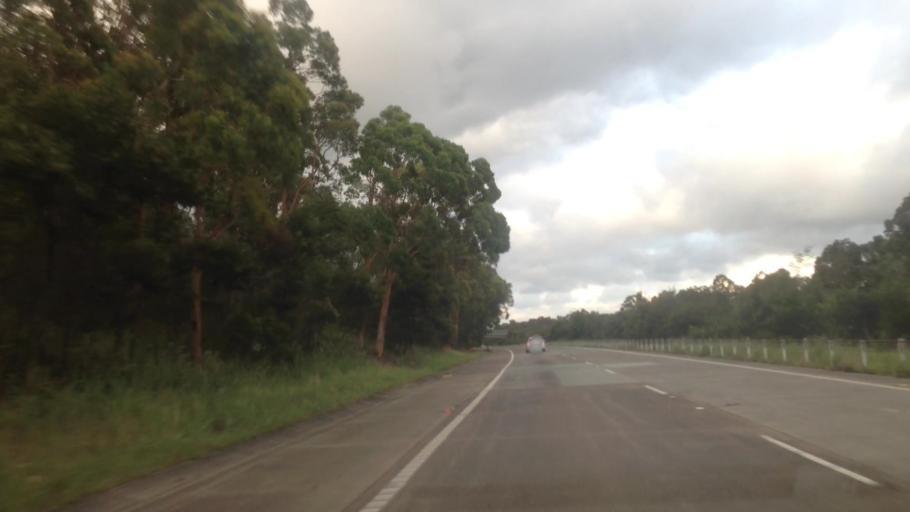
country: AU
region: New South Wales
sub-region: Wyong Shire
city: Charmhaven
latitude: -33.1985
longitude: 151.4634
